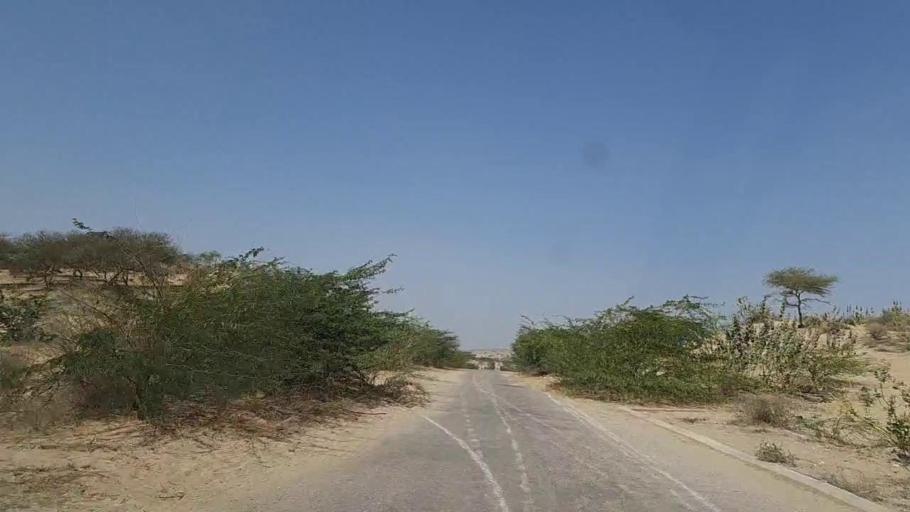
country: PK
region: Sindh
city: Naukot
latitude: 24.5837
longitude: 69.3189
